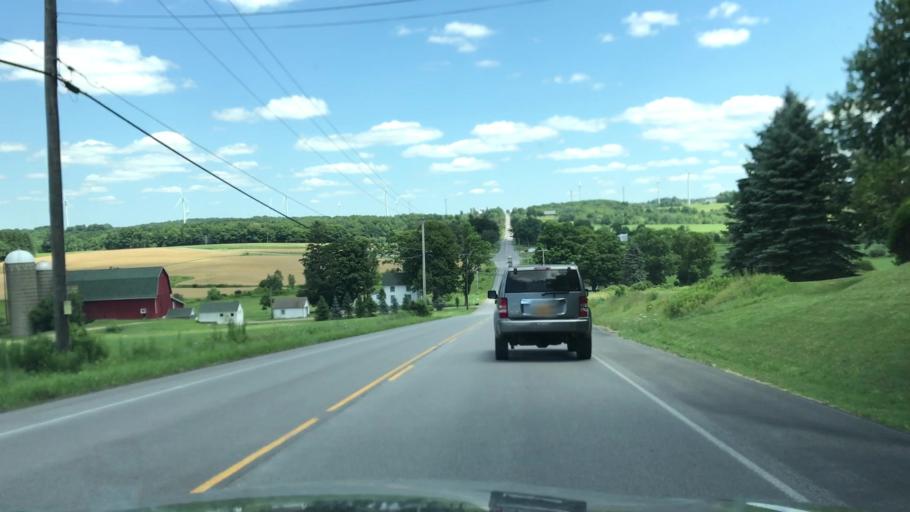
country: US
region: New York
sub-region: Erie County
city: Alden
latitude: 42.7696
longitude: -78.4524
